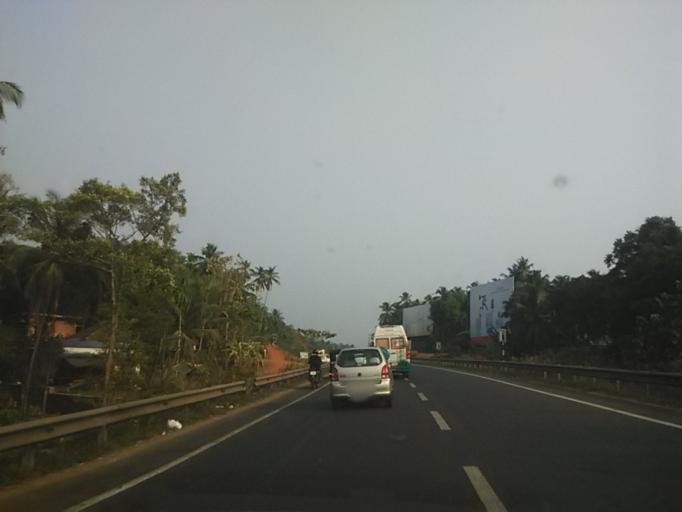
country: IN
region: Kerala
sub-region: Kozhikode
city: Kozhikode
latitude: 11.3087
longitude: 75.7852
